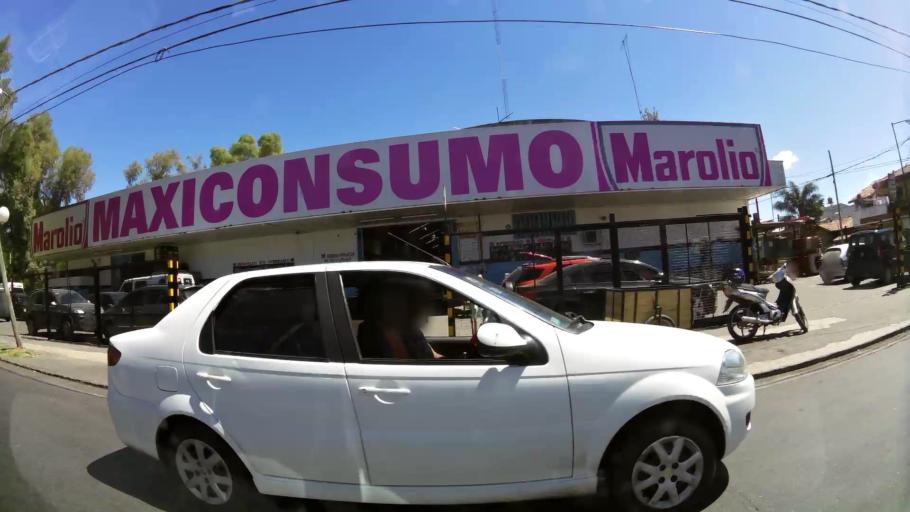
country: AR
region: Buenos Aires
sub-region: Partido de Tigre
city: Tigre
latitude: -34.5008
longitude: -58.5770
